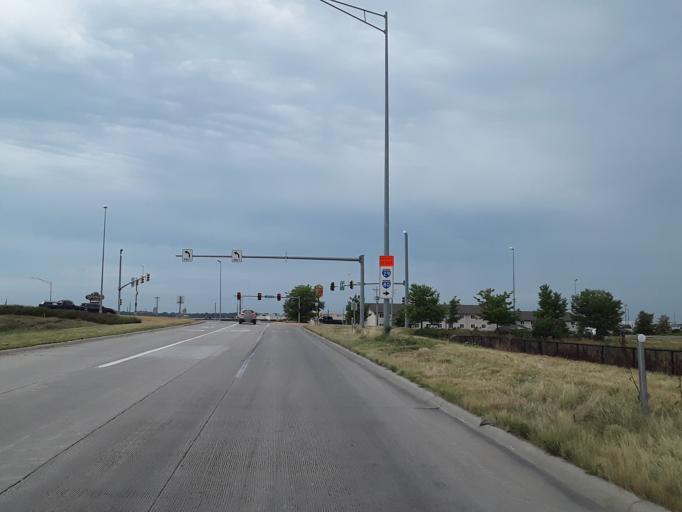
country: US
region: Iowa
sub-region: Pottawattamie County
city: Council Bluffs
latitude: 41.2332
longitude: -95.8779
